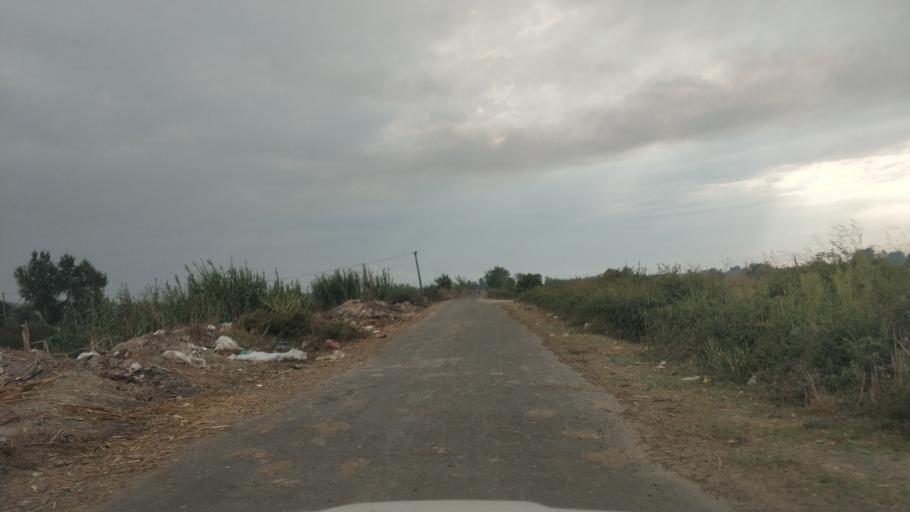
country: AL
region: Fier
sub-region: Rrethi i Fierit
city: Dermenas
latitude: 40.7298
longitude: 19.4647
